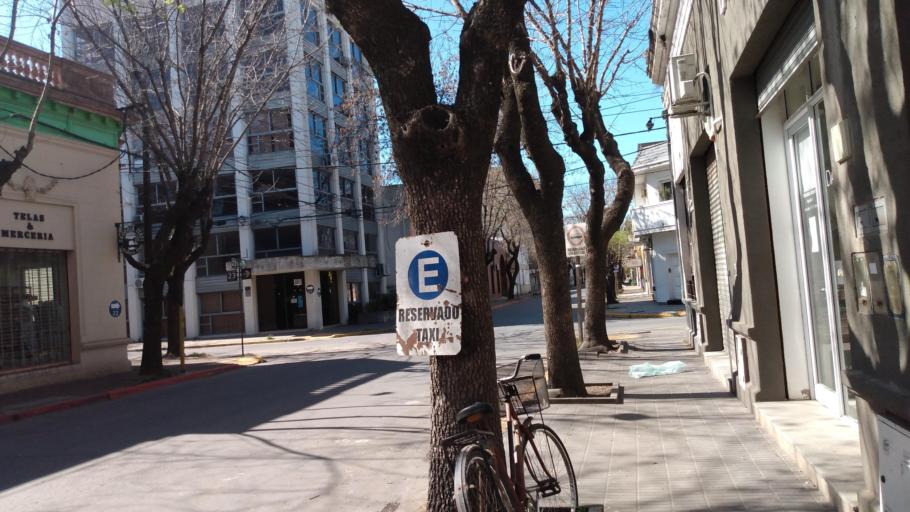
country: AR
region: Buenos Aires
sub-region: Partido de Mercedes
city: Mercedes
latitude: -34.6522
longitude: -59.4298
